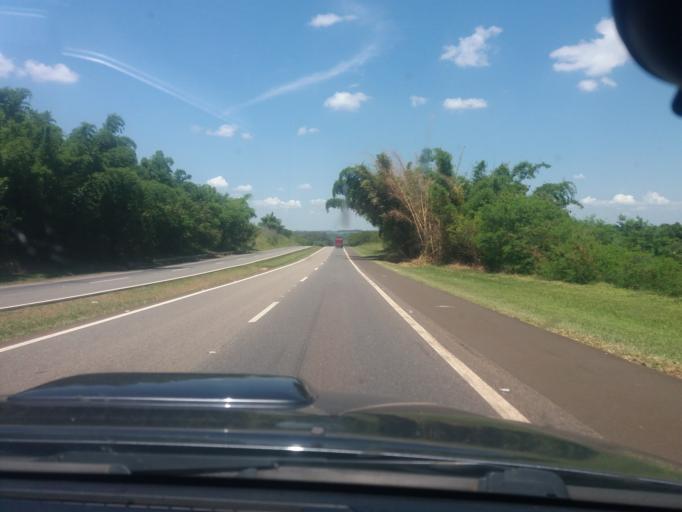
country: BR
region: Sao Paulo
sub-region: Tatui
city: Tatui
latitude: -23.3660
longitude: -47.9033
